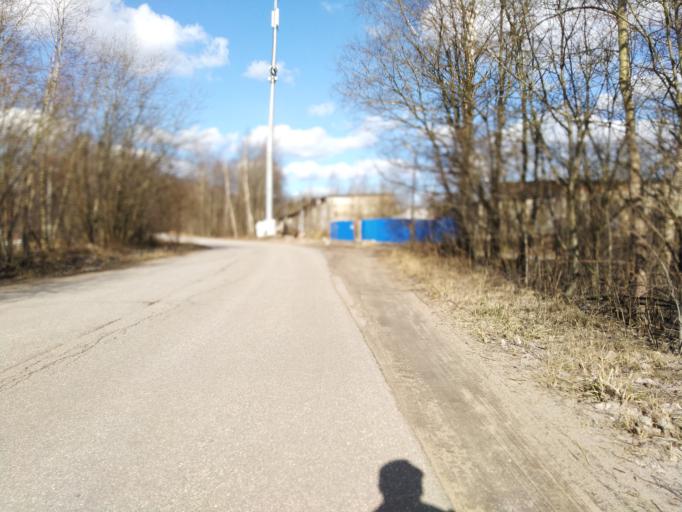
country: RU
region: Leningrad
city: Novoye Devyatkino
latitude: 60.1051
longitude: 30.4812
